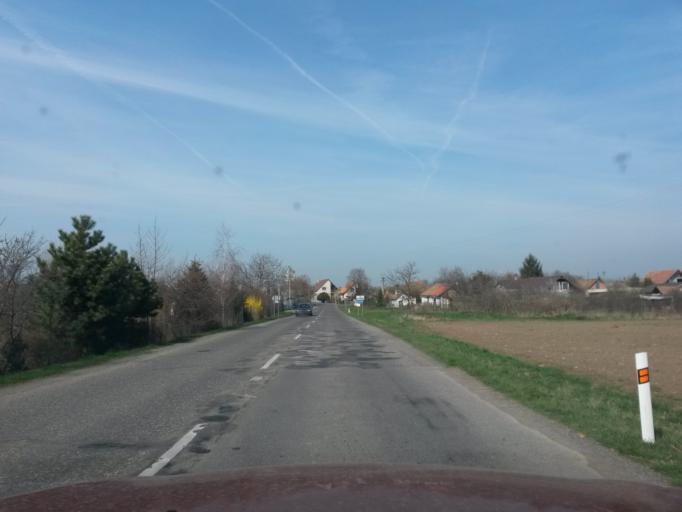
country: SK
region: Nitriansky
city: Zeliezovce
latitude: 48.1225
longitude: 18.6364
